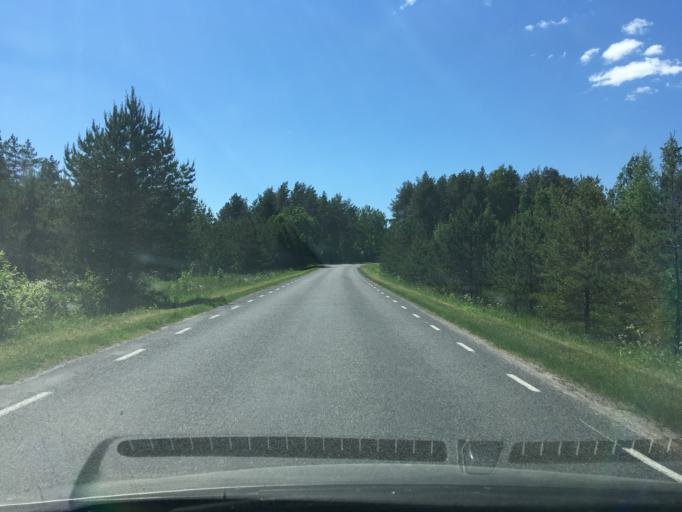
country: EE
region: Raplamaa
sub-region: Kohila vald
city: Kohila
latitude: 59.1128
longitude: 24.8279
